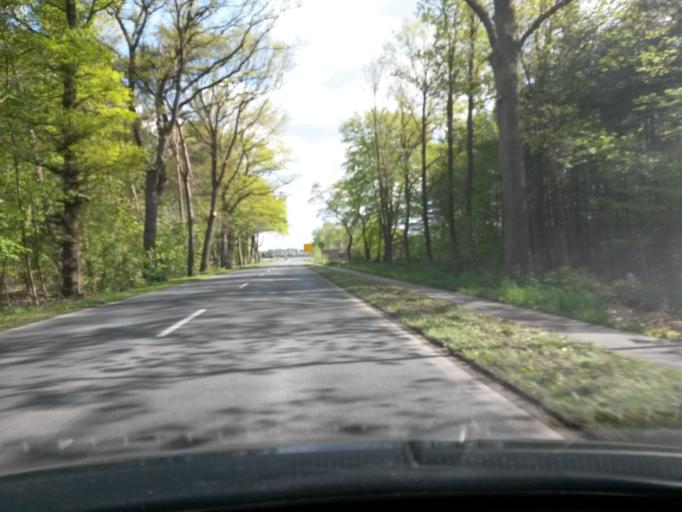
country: DE
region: North Rhine-Westphalia
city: Wegberg
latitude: 51.1853
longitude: 6.3409
